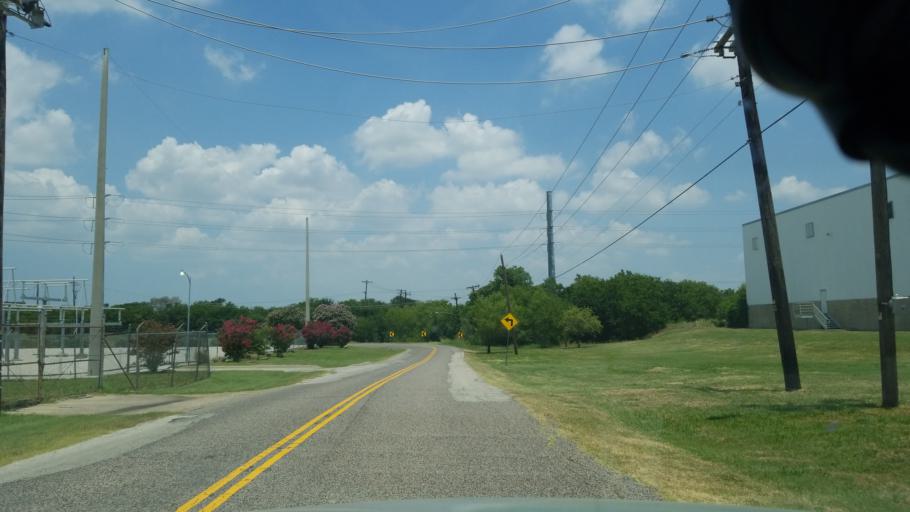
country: US
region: Texas
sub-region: Dallas County
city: Carrollton
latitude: 32.9586
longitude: -96.8684
